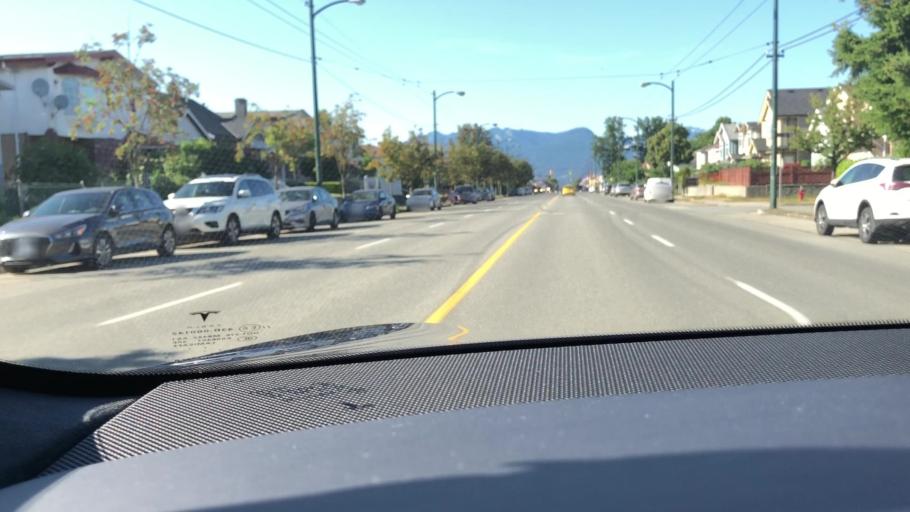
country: CA
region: British Columbia
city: Vancouver
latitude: 49.2281
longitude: -123.0657
